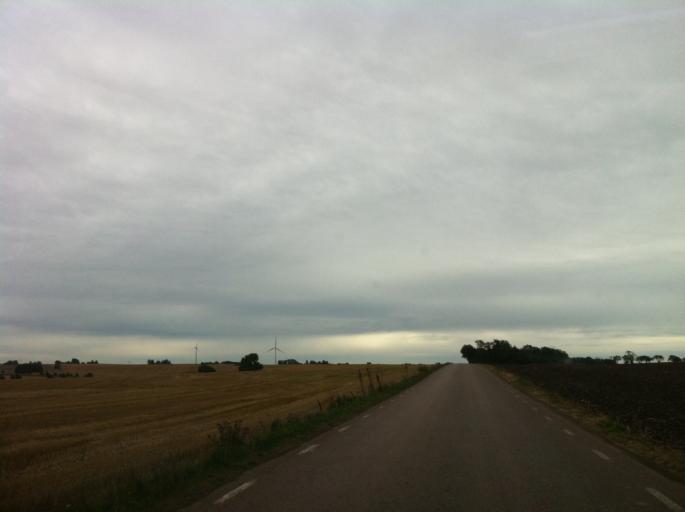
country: SE
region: Skane
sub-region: Landskrona
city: Asmundtorp
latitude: 55.9157
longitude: 13.0015
